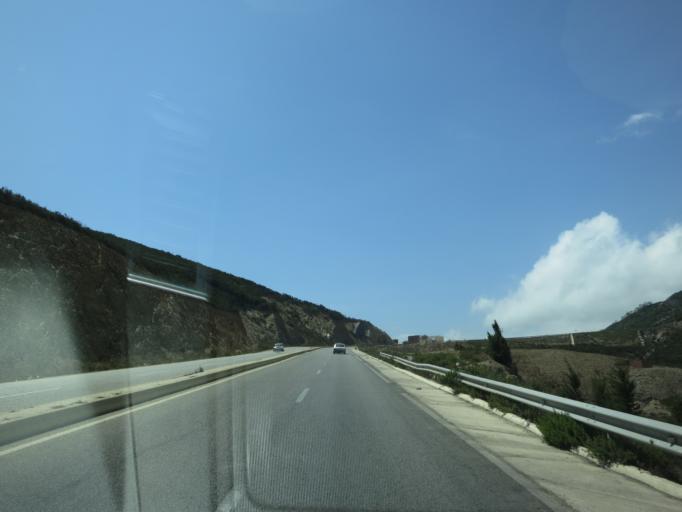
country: ES
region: Ceuta
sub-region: Ceuta
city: Ceuta
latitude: 35.8688
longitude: -5.3746
